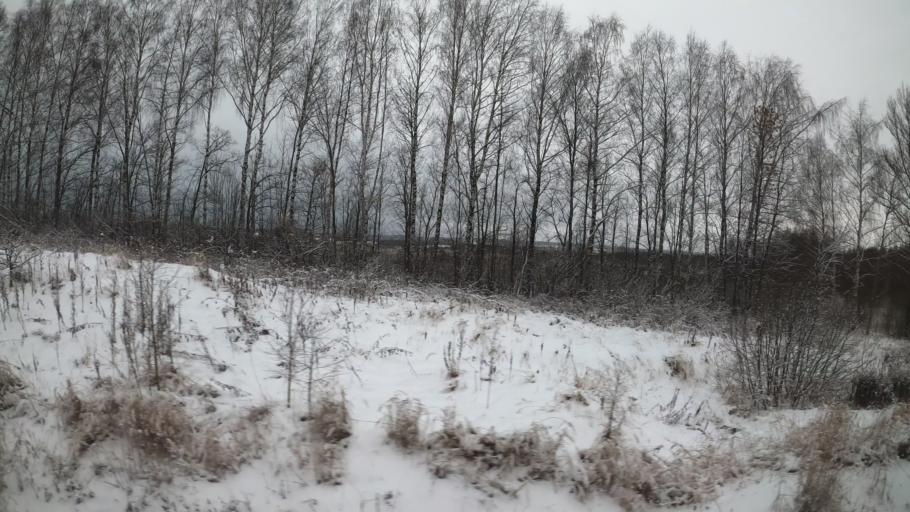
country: RU
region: Jaroslavl
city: Pereslavl'-Zalesskiy
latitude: 56.6876
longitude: 38.9186
